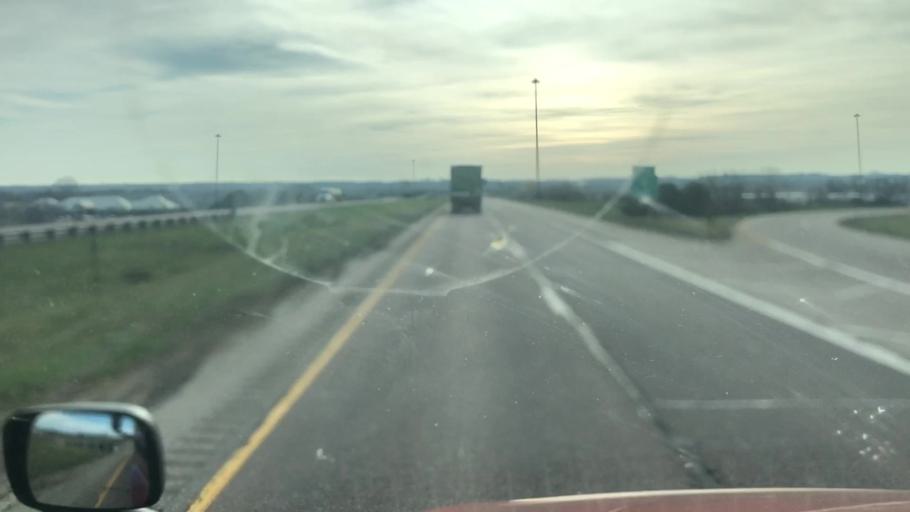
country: US
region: Nebraska
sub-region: Dakota County
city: South Sioux City
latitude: 42.4492
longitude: -96.4185
